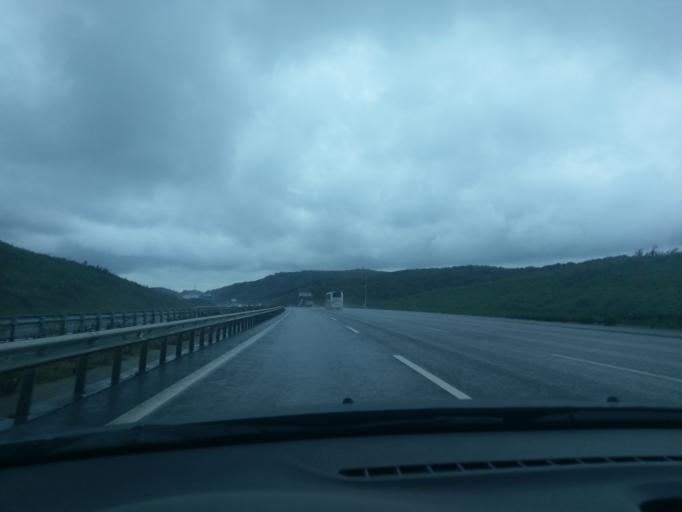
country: TR
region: Istanbul
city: Arikoey
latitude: 41.2303
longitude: 28.9355
